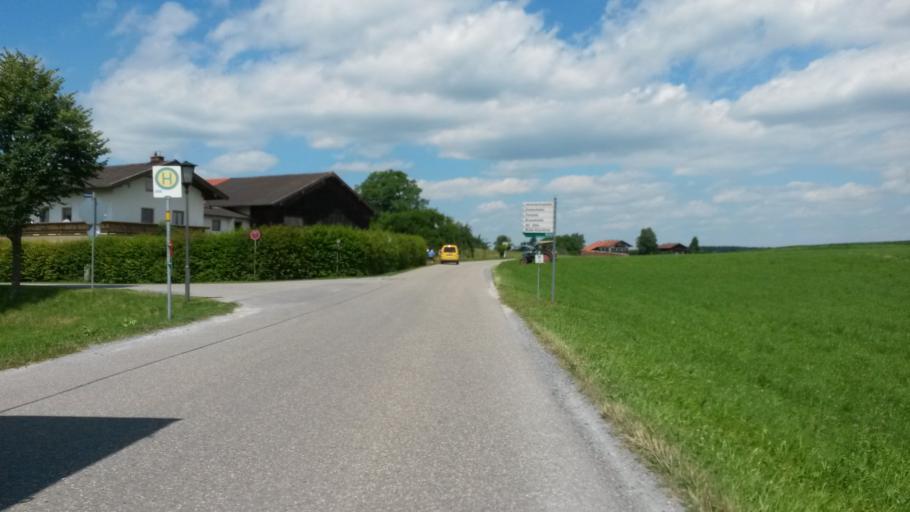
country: DE
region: Bavaria
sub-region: Upper Bavaria
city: Chieming
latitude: 47.8970
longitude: 12.5316
